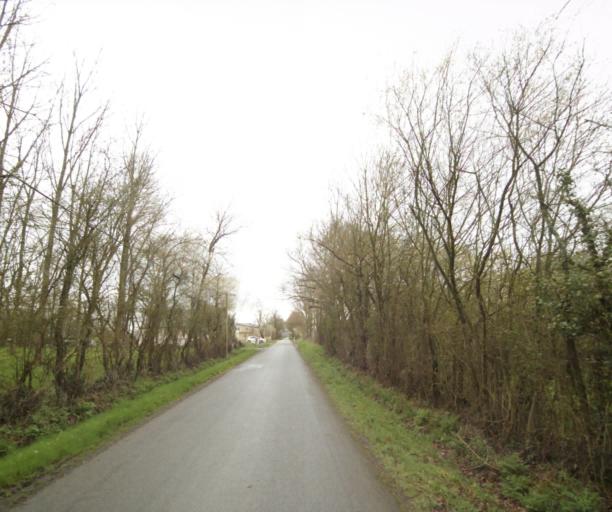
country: FR
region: Pays de la Loire
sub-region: Departement de la Loire-Atlantique
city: Bouvron
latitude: 47.4414
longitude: -1.8819
